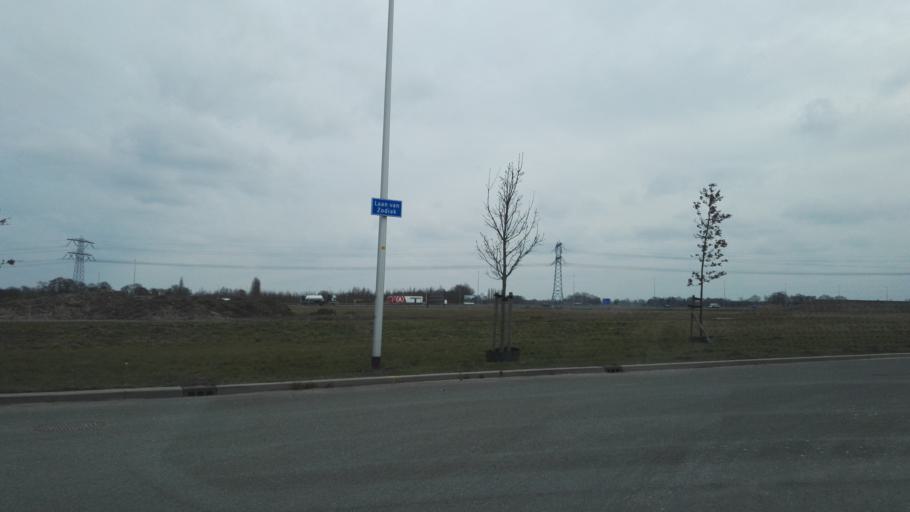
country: NL
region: Gelderland
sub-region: Gemeente Apeldoorn
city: Apeldoorn
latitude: 52.2476
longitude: 6.0035
